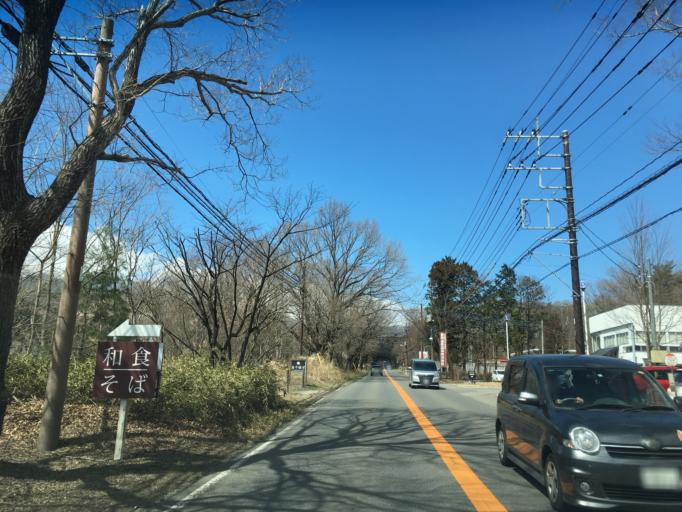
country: JP
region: Tochigi
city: Kuroiso
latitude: 37.0541
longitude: 140.0135
